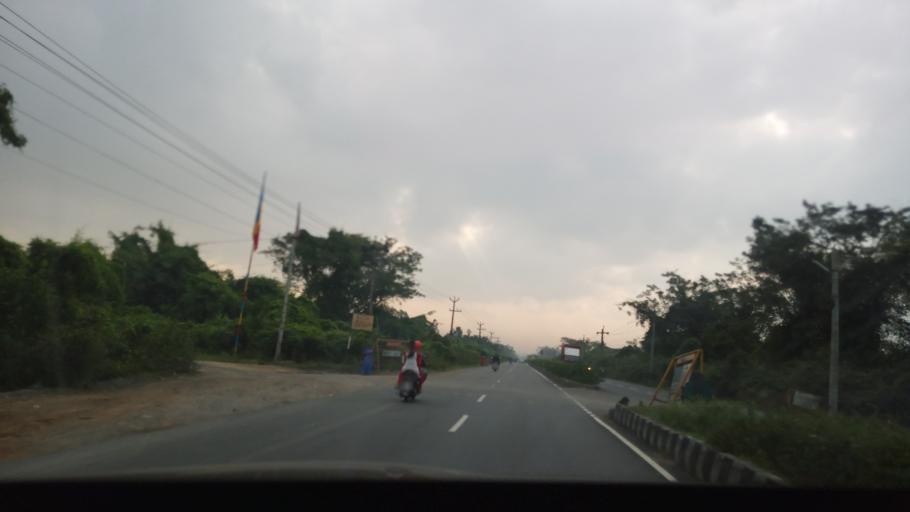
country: IN
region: Tamil Nadu
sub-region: Kancheepuram
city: Vengavasal
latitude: 12.8233
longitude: 80.1699
